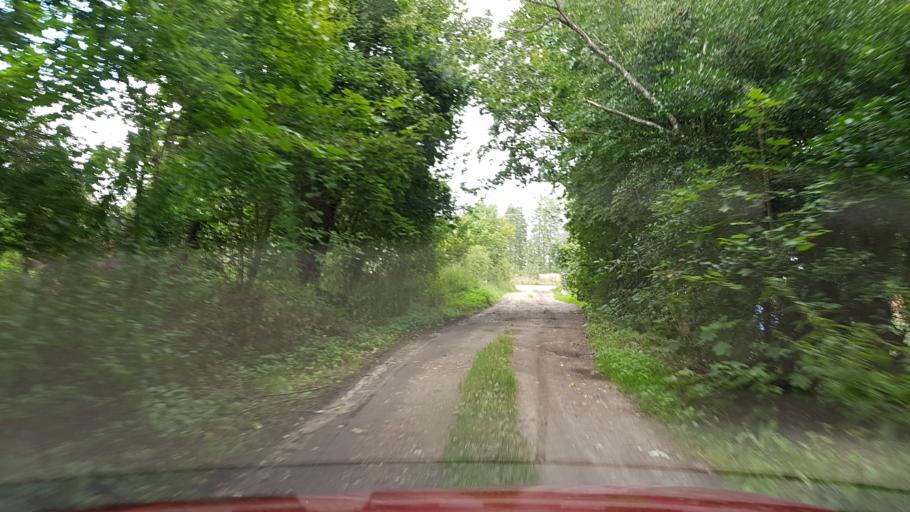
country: PL
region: West Pomeranian Voivodeship
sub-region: Powiat bialogardzki
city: Tychowo
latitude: 53.9802
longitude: 16.3891
